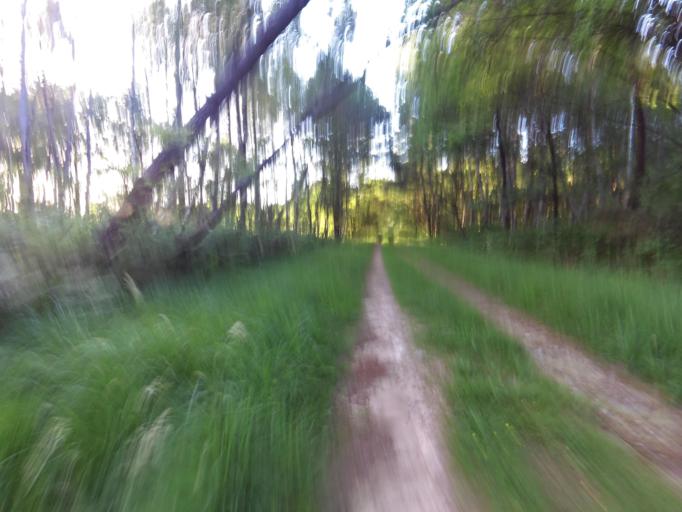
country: FR
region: Brittany
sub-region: Departement du Morbihan
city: Molac
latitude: 47.7487
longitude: -2.4144
